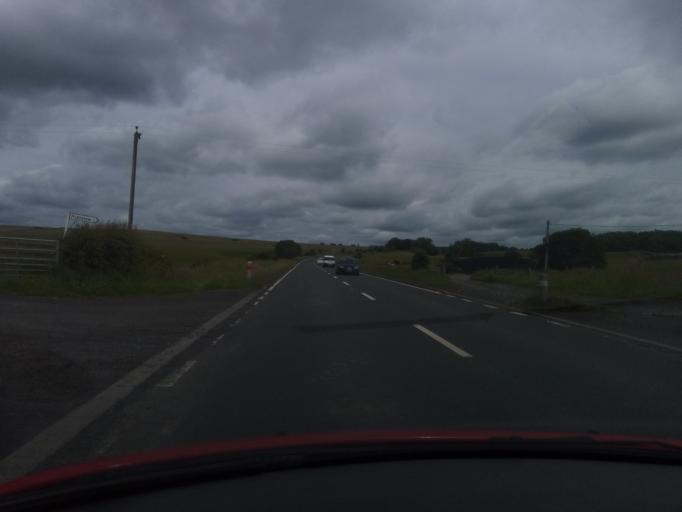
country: GB
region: Scotland
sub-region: The Scottish Borders
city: Hawick
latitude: 55.4517
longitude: -2.7785
